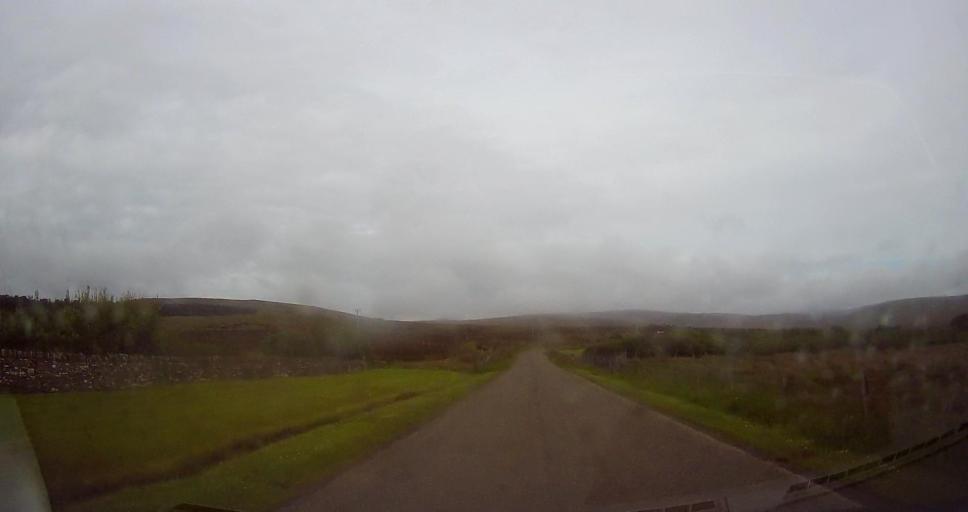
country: GB
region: Scotland
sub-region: Orkney Islands
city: Stromness
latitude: 58.8339
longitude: -3.2102
